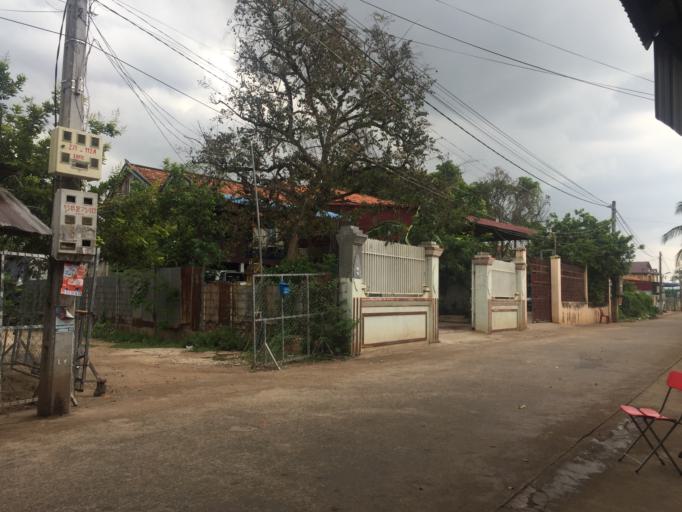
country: KH
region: Kandal
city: Ta Khmau
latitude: 11.5139
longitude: 105.0389
